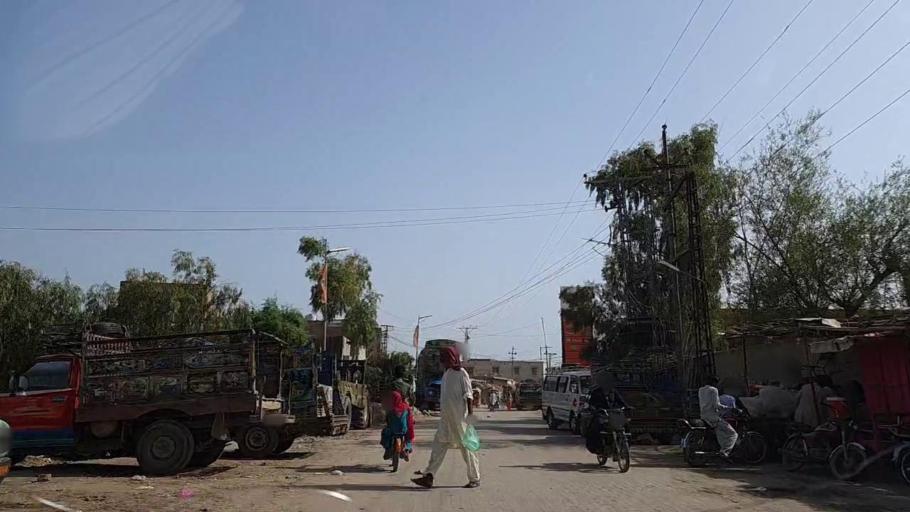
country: PK
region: Sindh
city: Kandiaro
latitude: 27.0574
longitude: 68.2077
